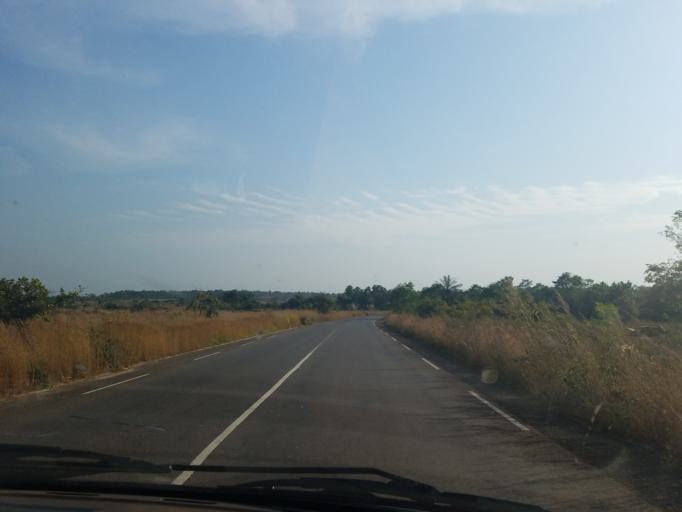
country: GN
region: Boke
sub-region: Boke Prefecture
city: Sangueya
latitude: 10.5019
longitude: -14.4049
